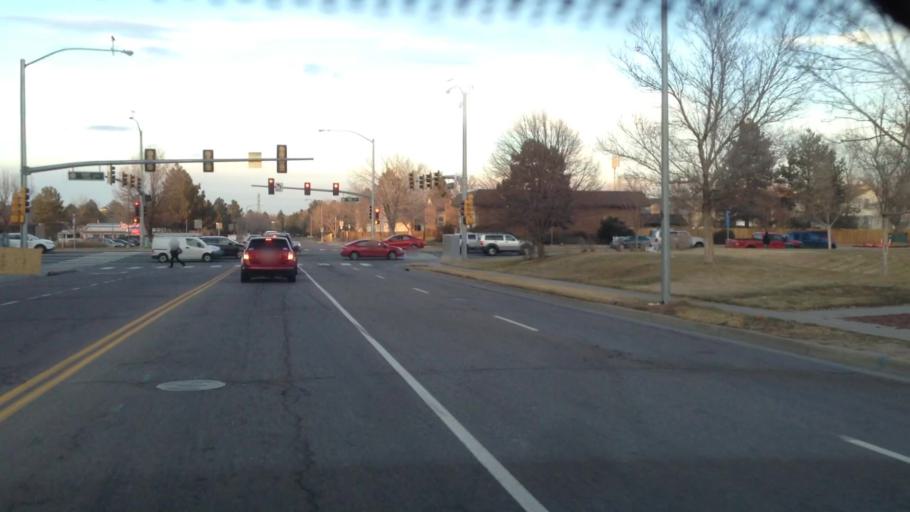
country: US
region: Colorado
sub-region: Adams County
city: Aurora
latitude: 39.6742
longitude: -104.8240
